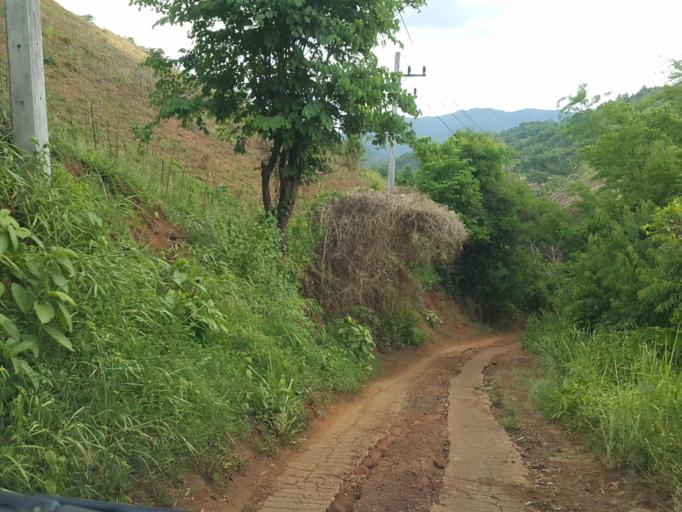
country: TH
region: Chiang Mai
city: Samoeng
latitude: 18.7820
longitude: 98.8246
